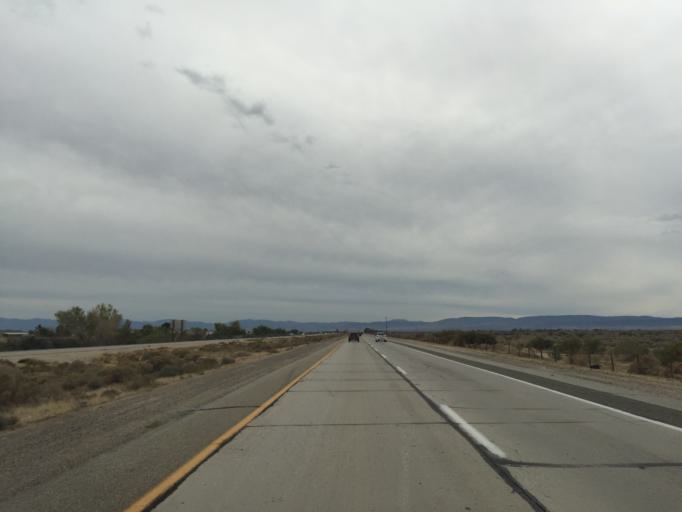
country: US
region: California
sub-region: Kern County
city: Rosamond
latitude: 34.8482
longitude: -118.1717
